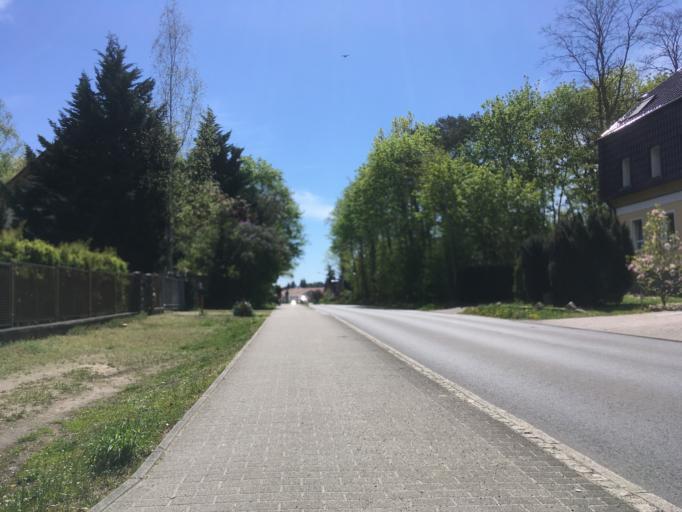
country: DE
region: Brandenburg
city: Wildau
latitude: 52.3254
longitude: 13.6135
